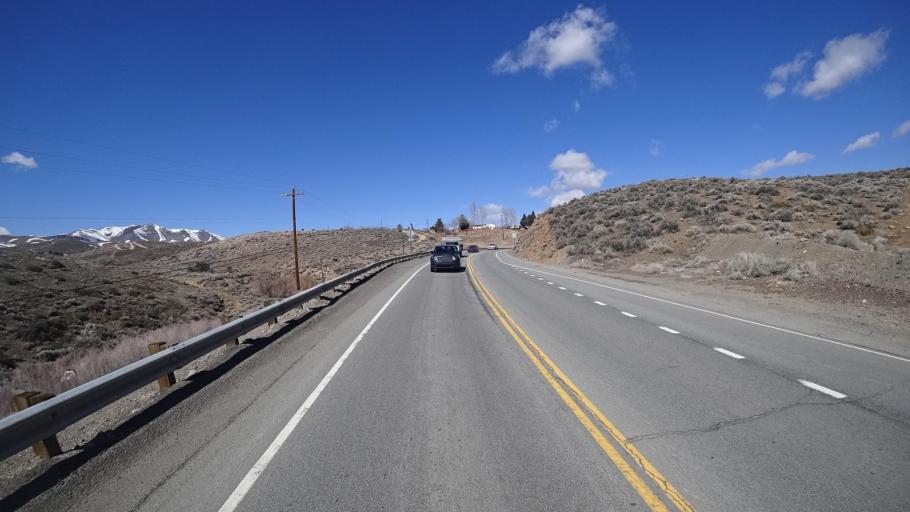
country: US
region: Nevada
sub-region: Washoe County
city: Golden Valley
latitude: 39.5875
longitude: -119.8339
